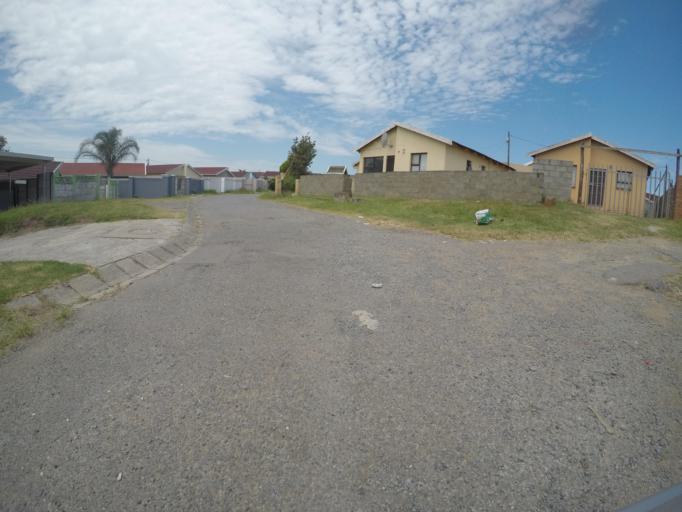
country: ZA
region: Eastern Cape
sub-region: Buffalo City Metropolitan Municipality
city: East London
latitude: -32.9907
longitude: 27.8684
